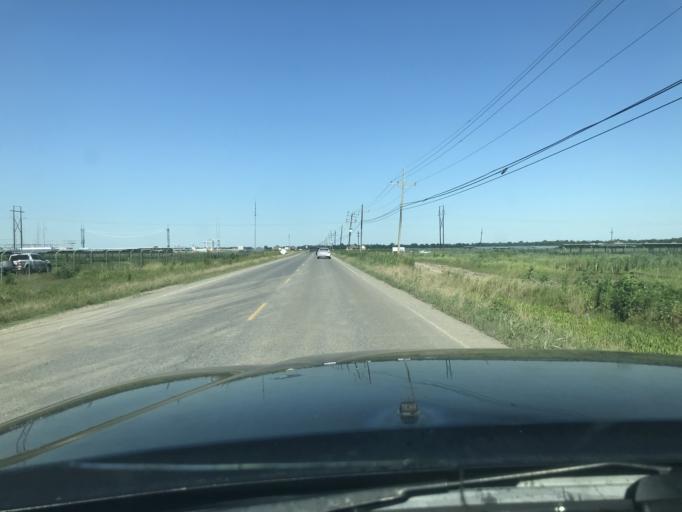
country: US
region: Louisiana
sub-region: West Baton Rouge Parish
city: Brusly
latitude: 30.4688
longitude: -91.3162
